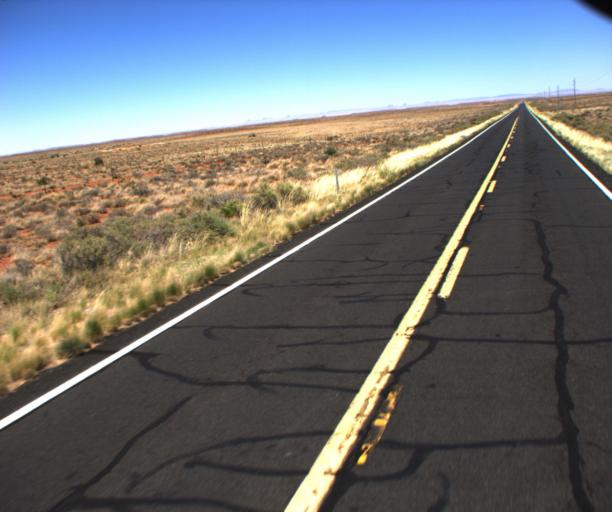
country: US
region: Arizona
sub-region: Coconino County
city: LeChee
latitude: 34.8838
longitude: -110.8799
